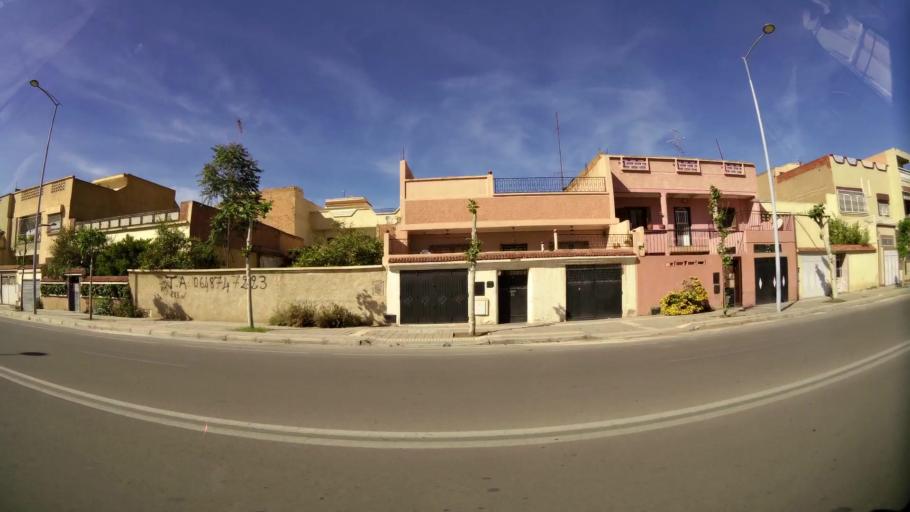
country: MA
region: Oriental
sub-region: Oujda-Angad
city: Oujda
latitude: 34.6657
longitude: -1.9143
